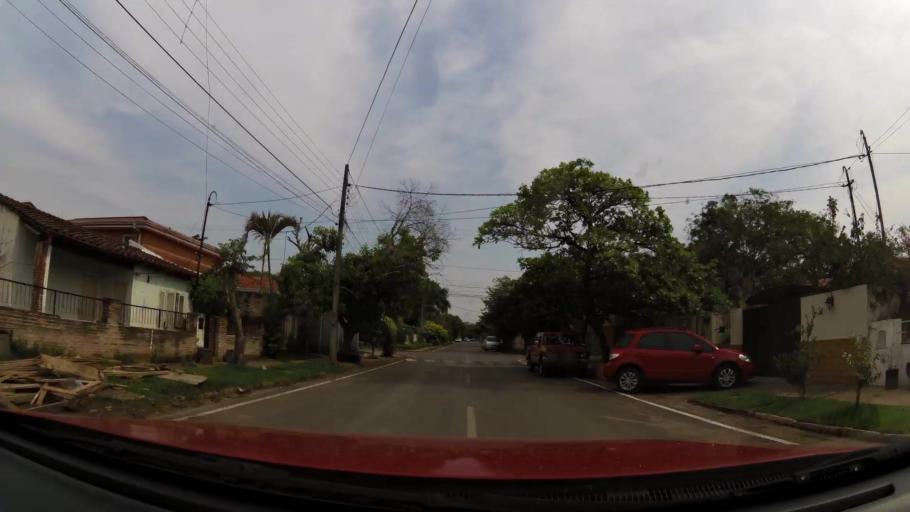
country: PY
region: Central
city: Fernando de la Mora
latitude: -25.2793
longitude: -57.5496
